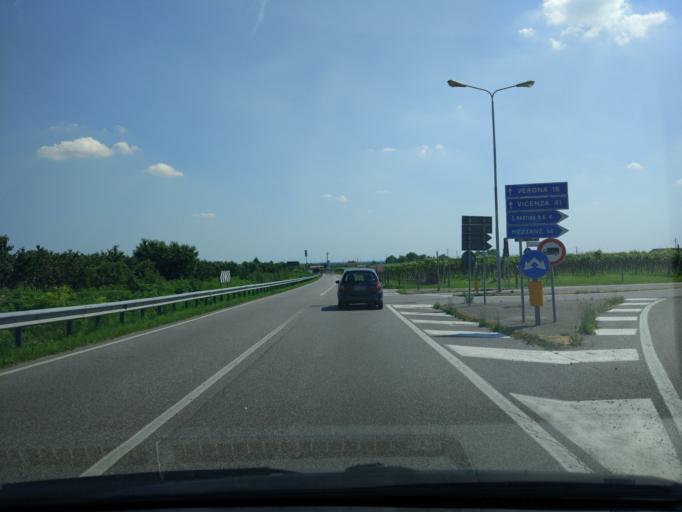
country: IT
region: Veneto
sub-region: Provincia di Verona
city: Colognola ai Colli
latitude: 45.4301
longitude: 11.1772
